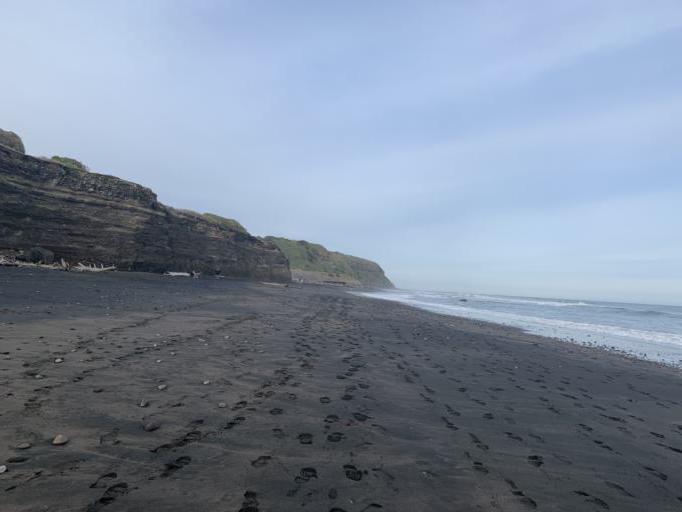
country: NZ
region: Taranaki
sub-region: South Taranaki District
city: Opunake
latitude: -39.5654
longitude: 174.0564
